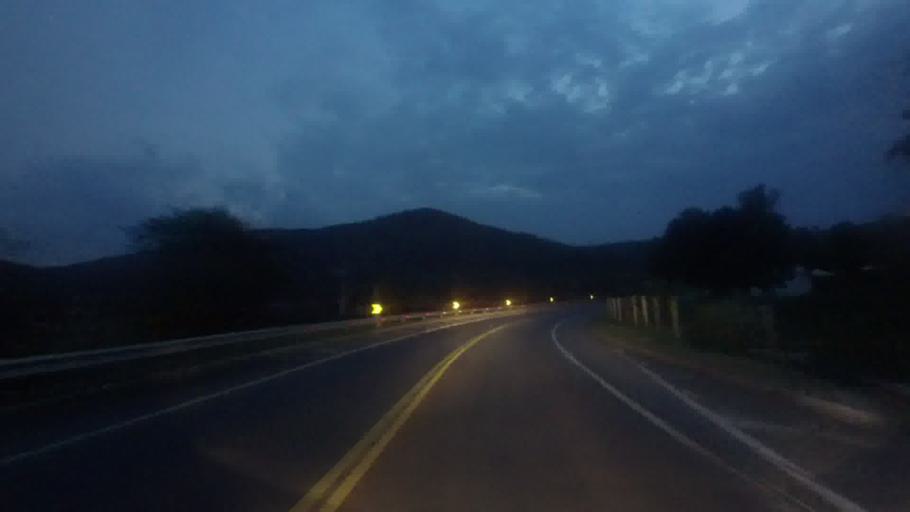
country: BR
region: Rio de Janeiro
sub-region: Sapucaia
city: Sapucaia
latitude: -21.9596
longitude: -42.8509
